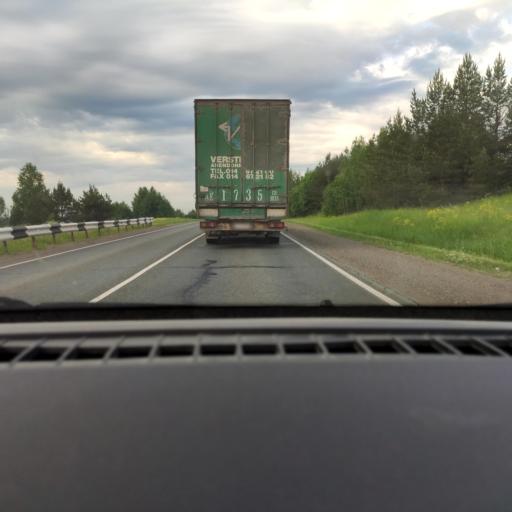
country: RU
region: Perm
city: Chastyye
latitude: 57.3782
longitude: 54.4363
